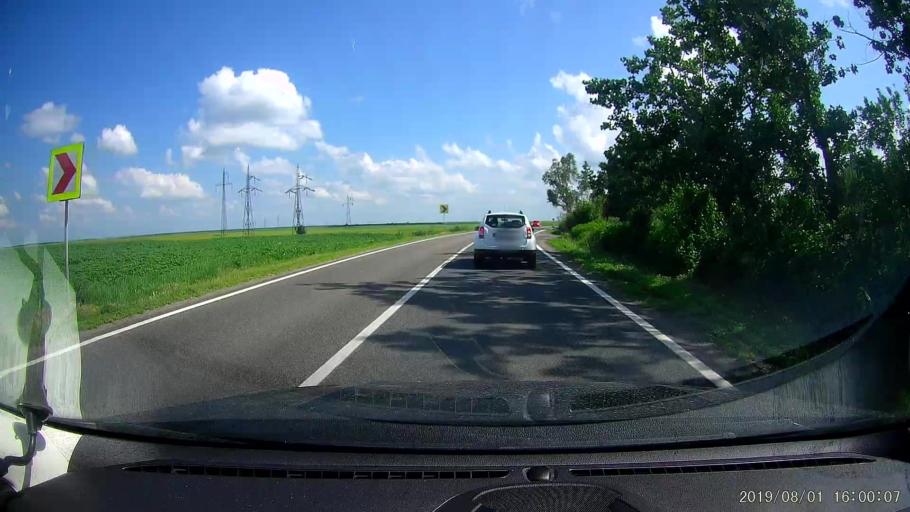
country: RO
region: Ialomita
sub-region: Comuna Ciulnita
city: Ciulnita
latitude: 44.5355
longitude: 27.3882
